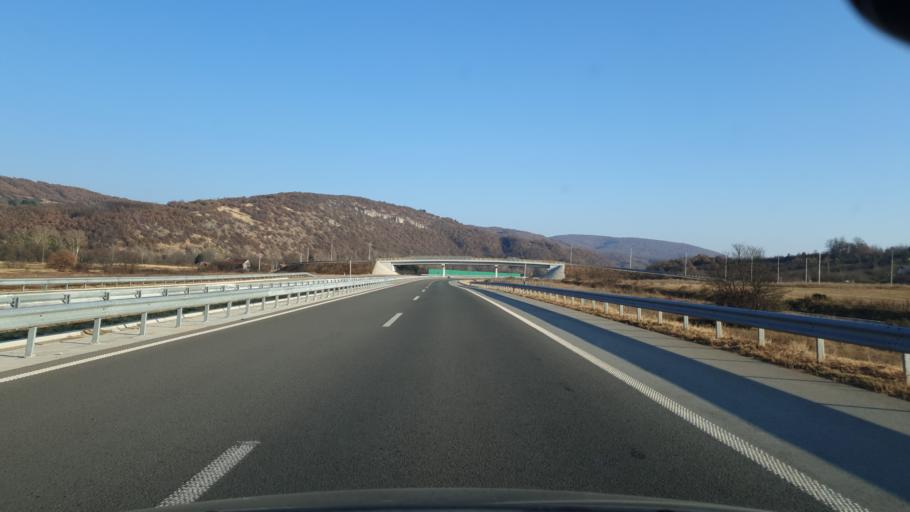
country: RS
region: Central Serbia
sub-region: Pirotski Okrug
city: Dimitrovgrad
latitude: 43.0603
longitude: 22.6865
